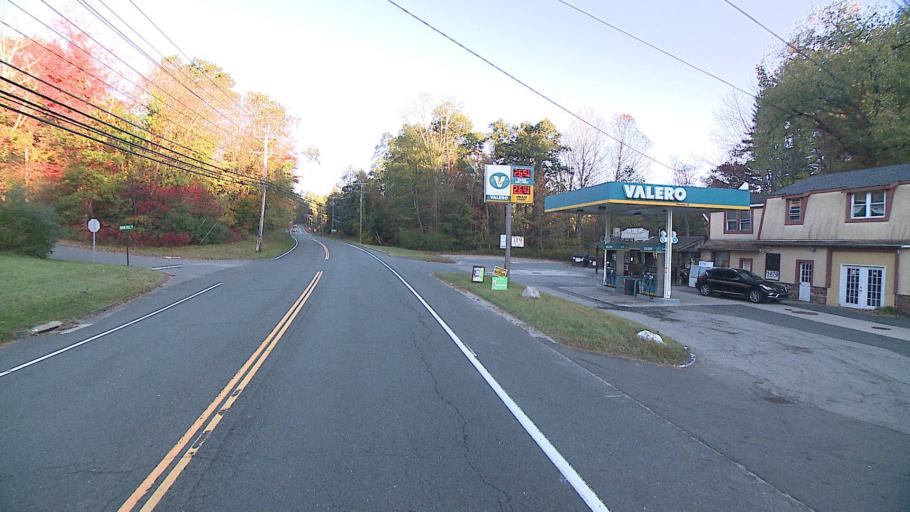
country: US
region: Connecticut
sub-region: Litchfield County
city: New Hartford Center
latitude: 41.9064
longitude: -72.9989
